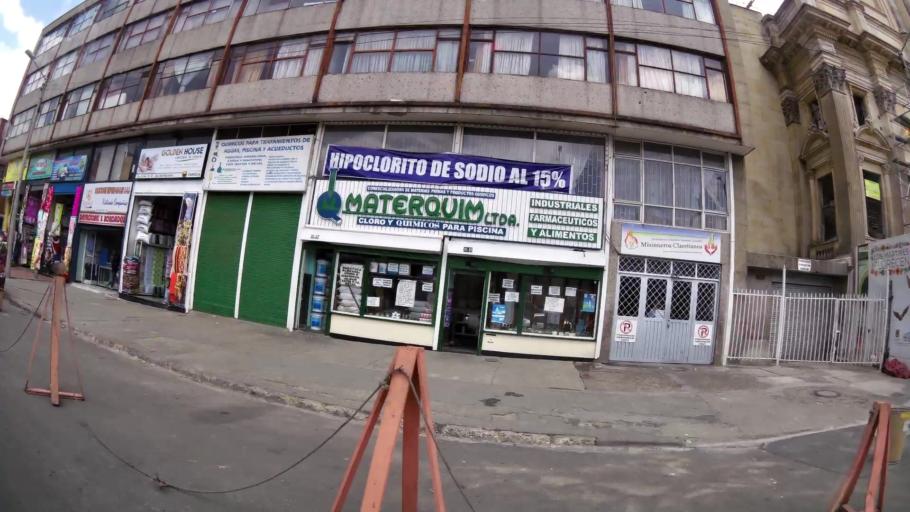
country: CO
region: Bogota D.C.
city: Bogota
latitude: 4.6020
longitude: -74.0823
